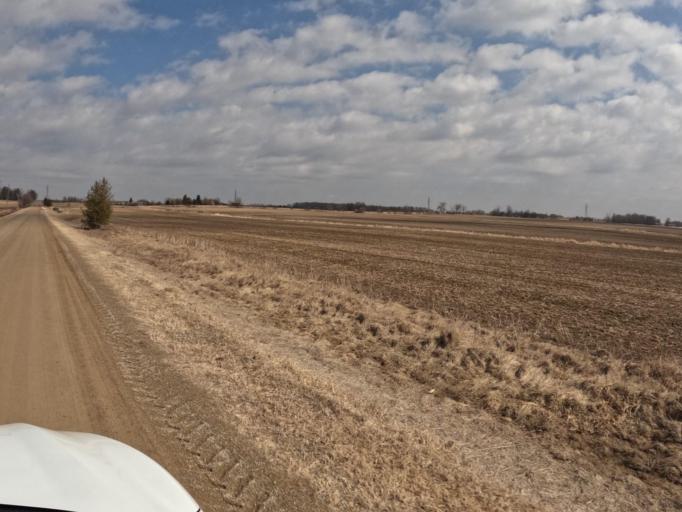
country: CA
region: Ontario
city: Orangeville
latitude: 43.9311
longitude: -80.2417
